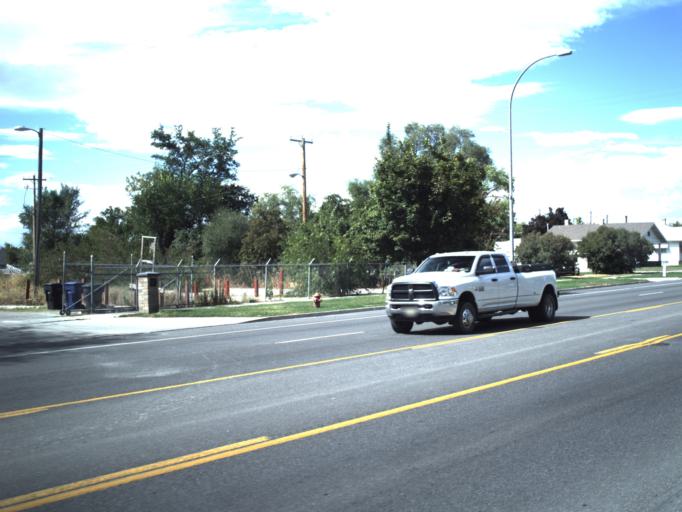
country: US
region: Utah
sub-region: Cache County
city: Smithfield
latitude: 41.8258
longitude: -111.8329
